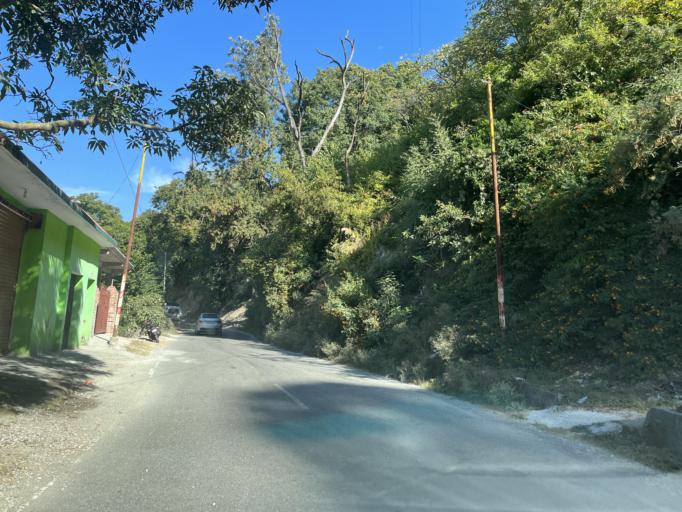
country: IN
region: Uttarakhand
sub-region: Naini Tal
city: Naini Tal
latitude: 29.5215
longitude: 79.4820
